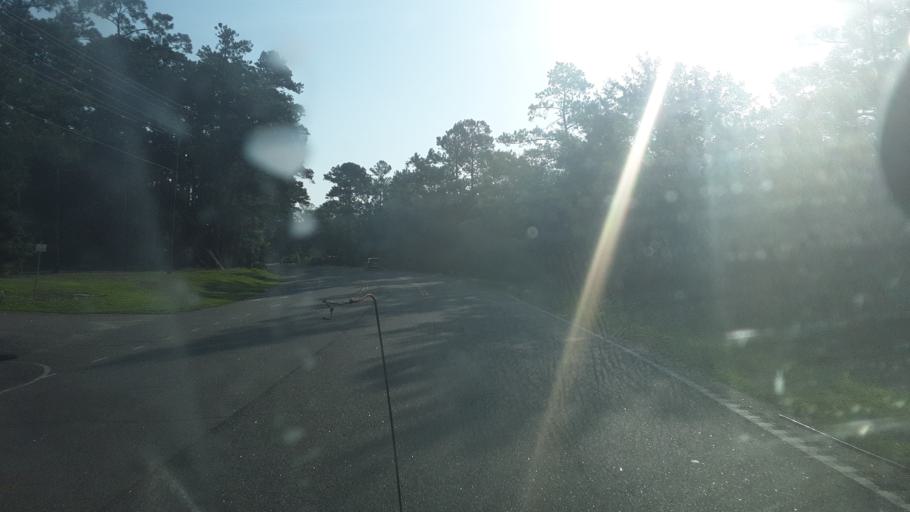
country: US
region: South Carolina
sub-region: Horry County
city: Forestbrook
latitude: 33.8218
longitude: -78.9038
